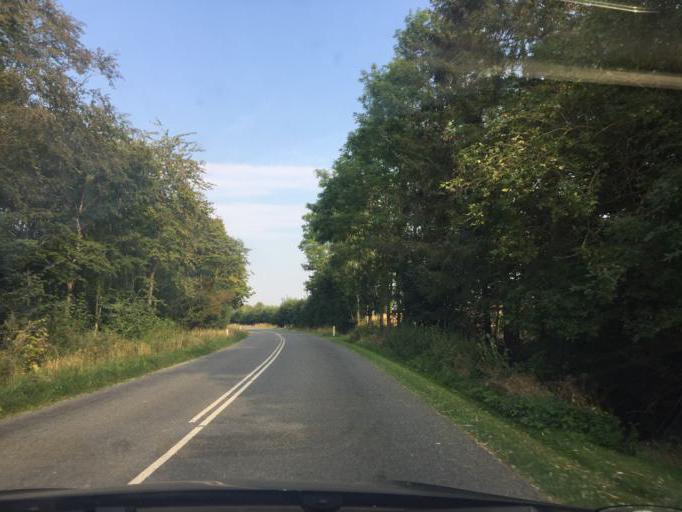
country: DK
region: South Denmark
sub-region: Faaborg-Midtfyn Kommune
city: Arslev
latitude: 55.2801
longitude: 10.5080
